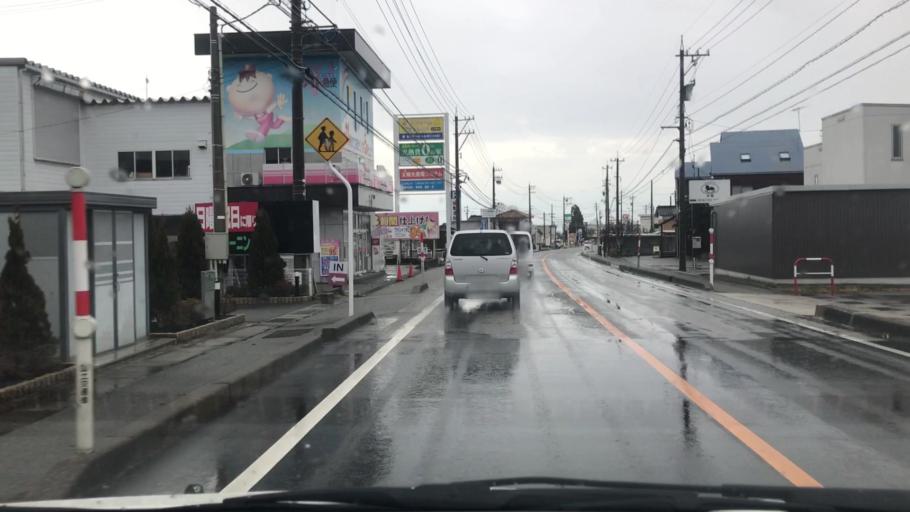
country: JP
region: Toyama
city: Yatsuomachi-higashikumisaka
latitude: 36.6026
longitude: 137.2033
